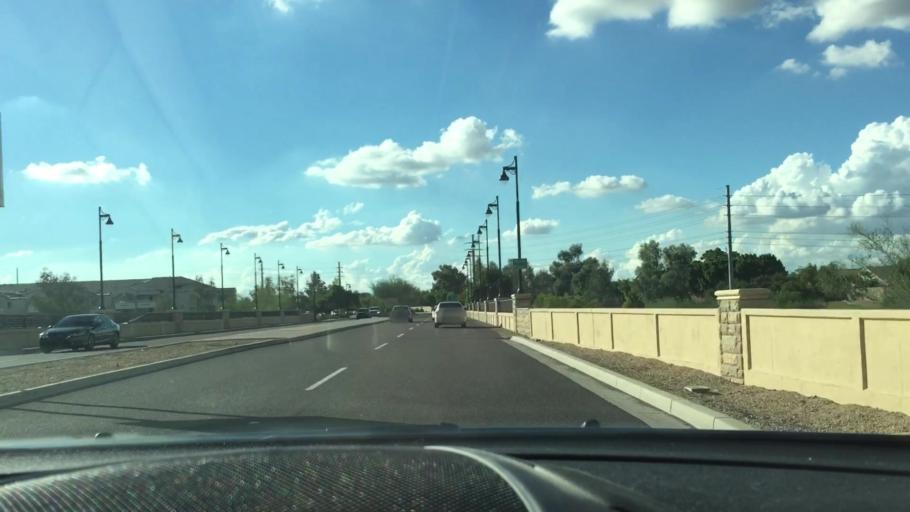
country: US
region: Arizona
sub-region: Maricopa County
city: Sun City
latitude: 33.6662
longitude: -112.2302
